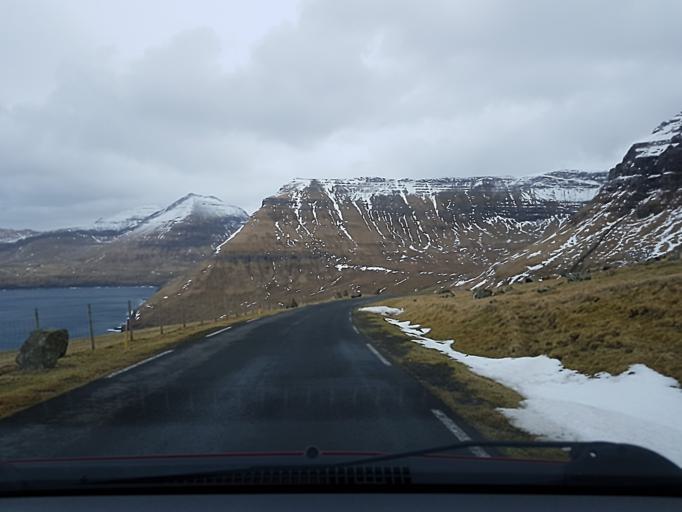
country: FO
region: Streymoy
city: Kollafjordhur
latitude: 62.0137
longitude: -6.9102
